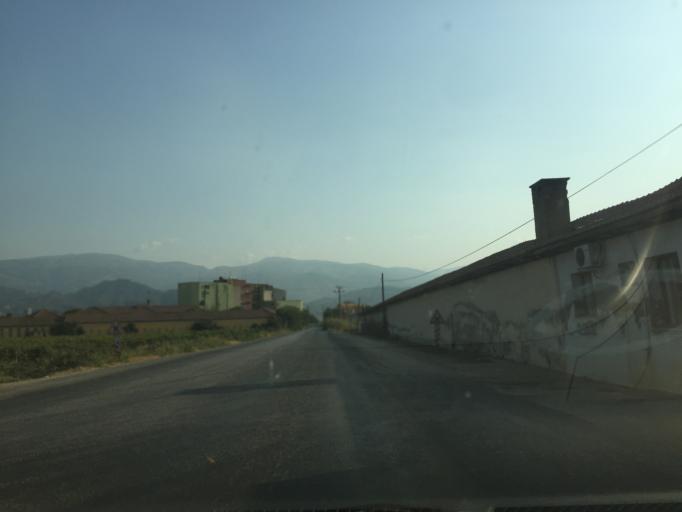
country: TR
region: Manisa
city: Salihli
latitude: 38.4980
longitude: 28.1831
